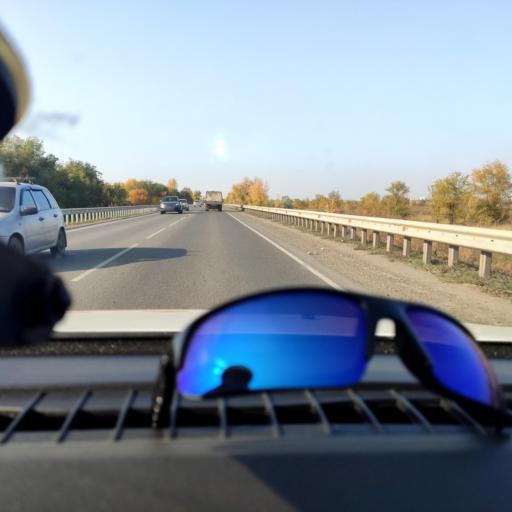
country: RU
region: Samara
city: Samara
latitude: 53.1091
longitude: 50.1320
